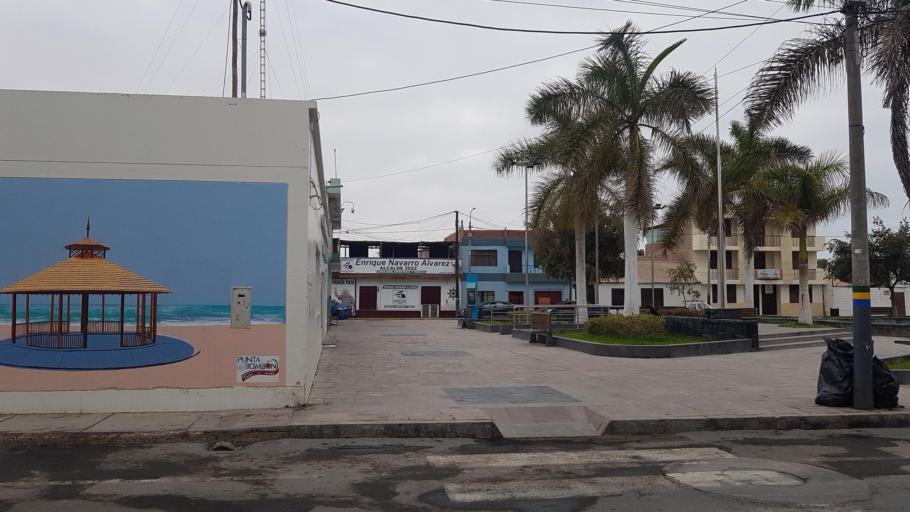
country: PE
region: Arequipa
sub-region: Provincia de Islay
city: Punta de Bombon
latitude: -17.1719
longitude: -71.7906
